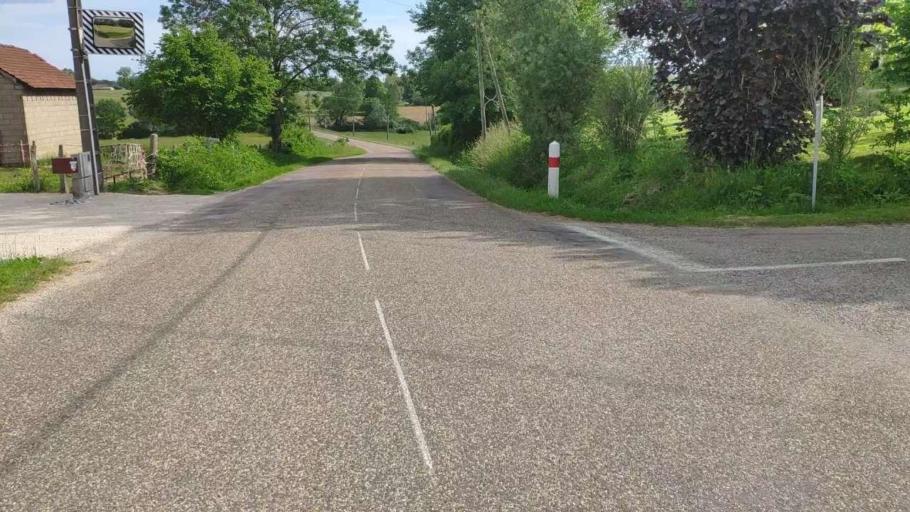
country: FR
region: Bourgogne
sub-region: Departement de Saone-et-Loire
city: Saint-Germain-du-Bois
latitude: 46.8058
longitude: 5.3401
